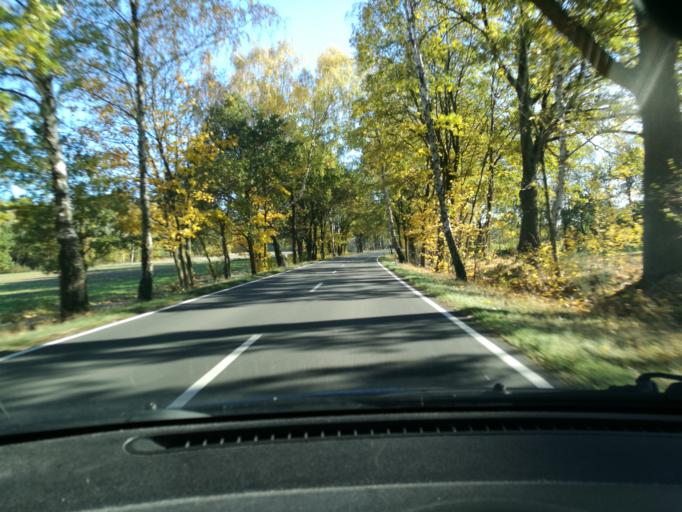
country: DE
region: Lower Saxony
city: Nahrendorf
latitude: 53.1541
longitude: 10.8257
